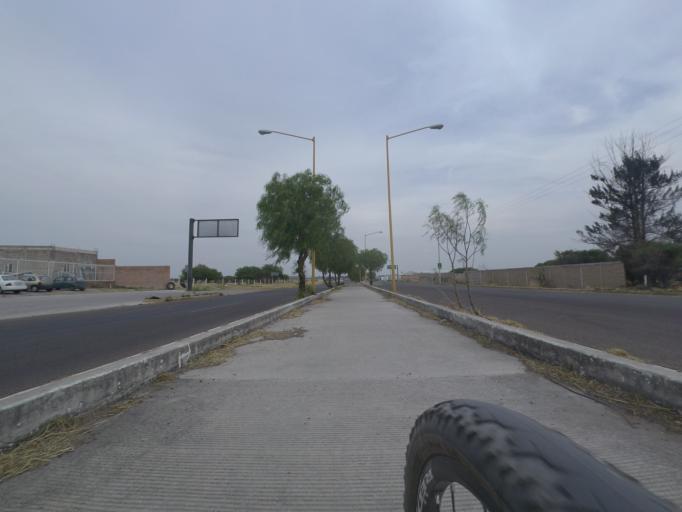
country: MX
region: Aguascalientes
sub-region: Aguascalientes
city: La Loma de los Negritos
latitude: 21.8610
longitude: -102.3678
